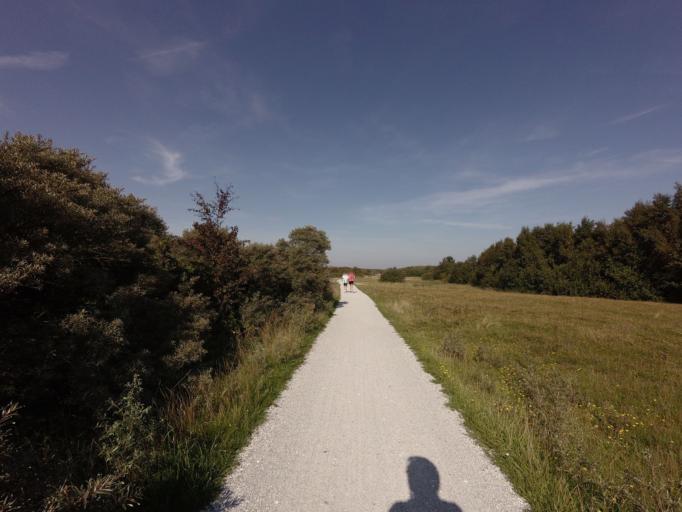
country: NL
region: Friesland
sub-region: Gemeente Schiermonnikoog
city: Schiermonnikoog
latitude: 53.4708
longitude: 6.1482
